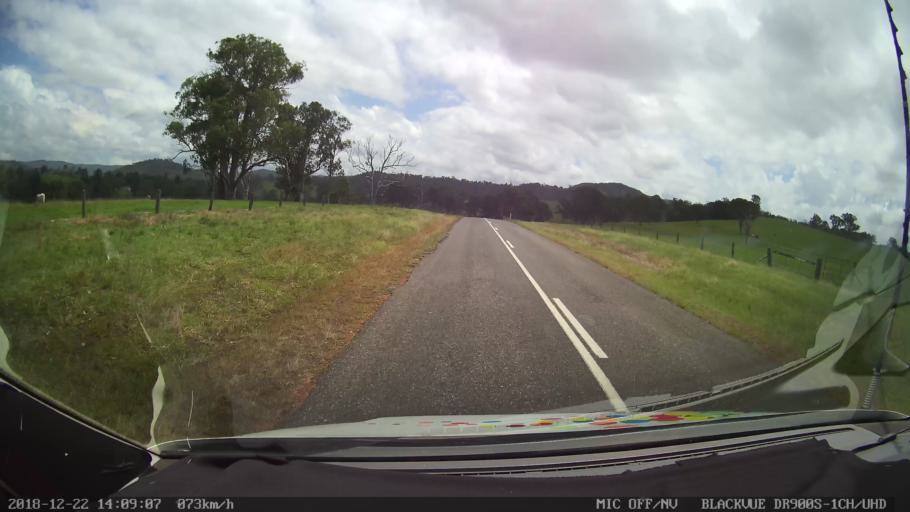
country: AU
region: New South Wales
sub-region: Clarence Valley
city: Coutts Crossing
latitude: -29.9842
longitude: 152.7204
